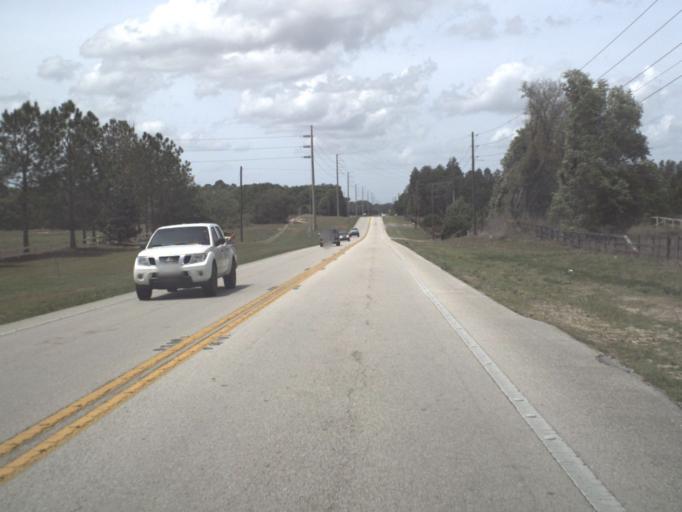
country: US
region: Florida
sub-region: Lake County
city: Mount Plymouth
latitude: 28.8512
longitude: -81.5696
